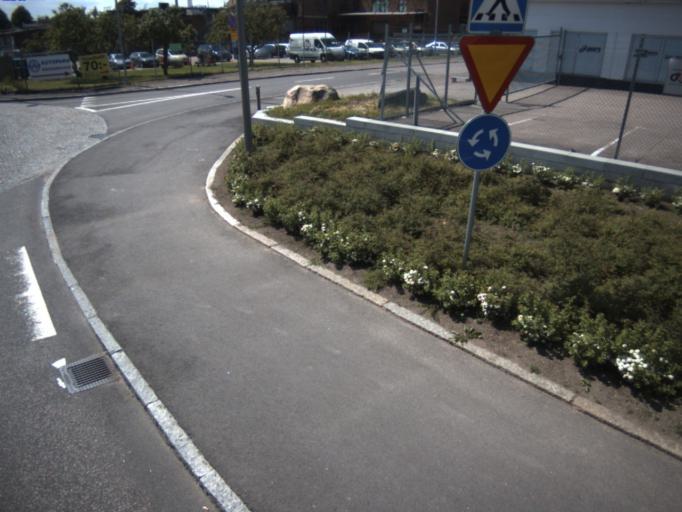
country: SE
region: Skane
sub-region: Helsingborg
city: Helsingborg
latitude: 56.0589
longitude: 12.7076
